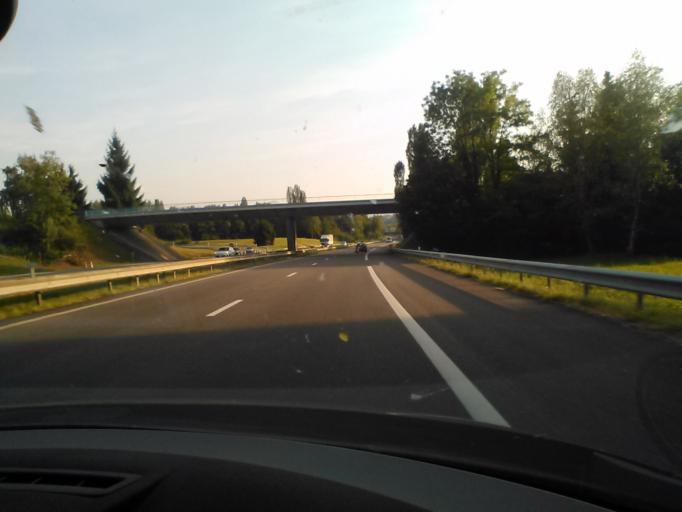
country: FR
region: Rhone-Alpes
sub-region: Departement de la Savoie
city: Drumettaz-Clarafond
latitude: 45.6535
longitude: 5.9255
